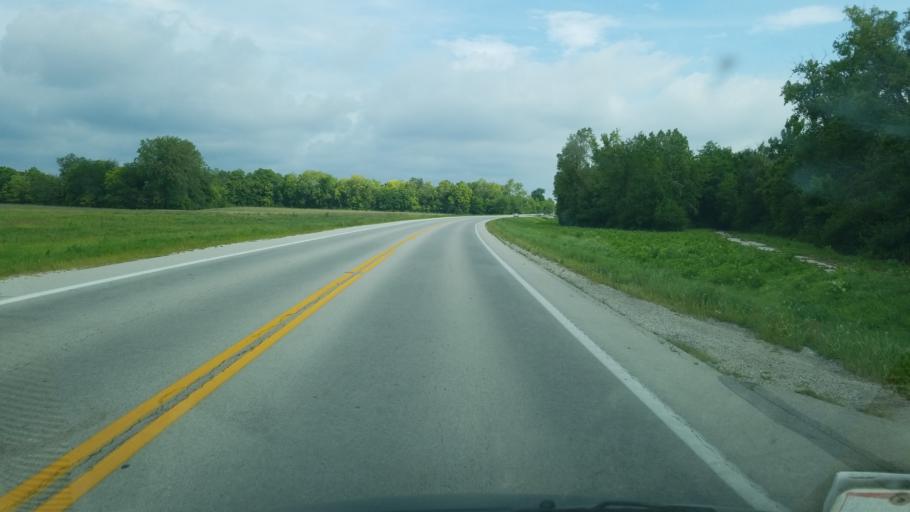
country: US
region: Ohio
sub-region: Sandusky County
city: Ballville
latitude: 41.2861
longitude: -83.1713
